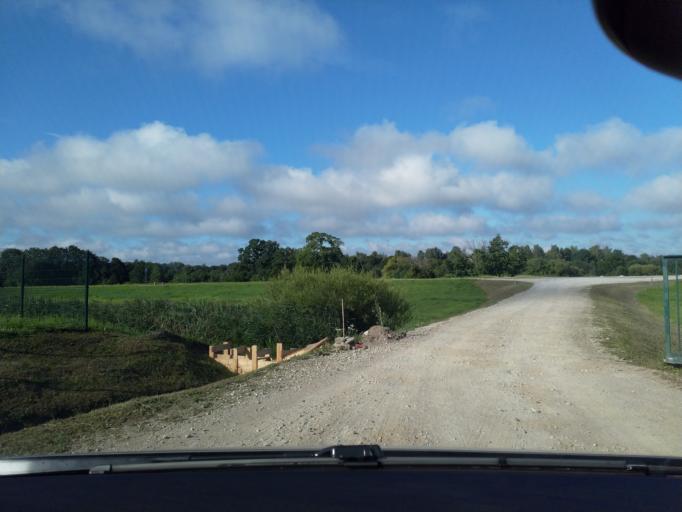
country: LV
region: Kuldigas Rajons
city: Kuldiga
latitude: 56.9565
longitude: 22.0078
